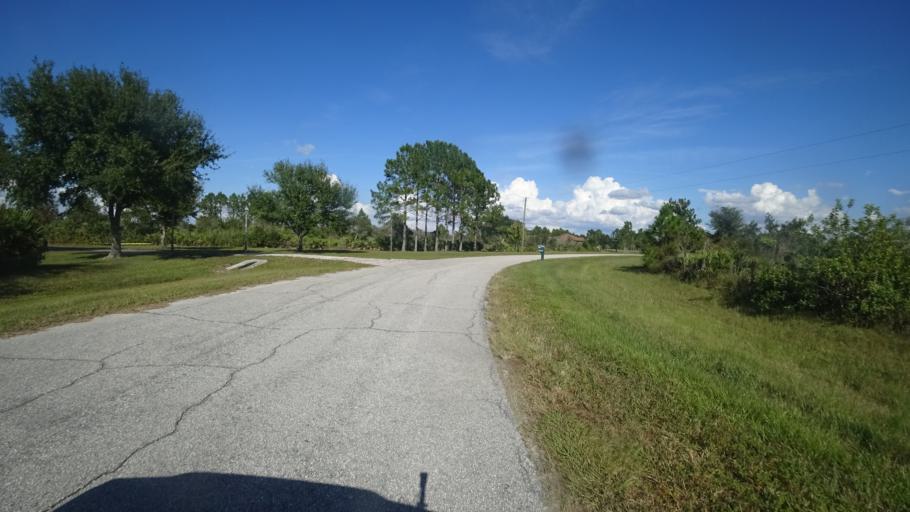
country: US
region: Florida
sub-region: Sarasota County
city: The Meadows
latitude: 27.4164
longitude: -82.2819
